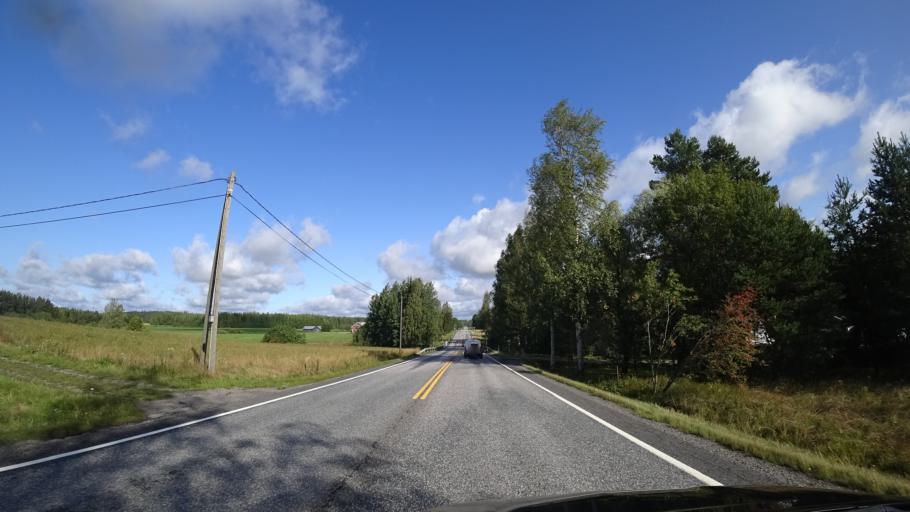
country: FI
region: Uusimaa
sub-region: Helsinki
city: Tuusula
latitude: 60.4614
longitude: 24.9475
